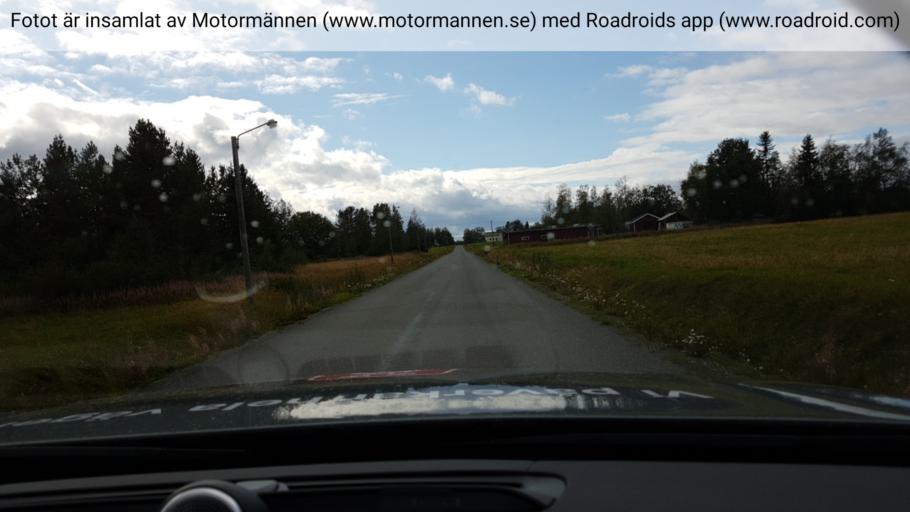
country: SE
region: Jaemtland
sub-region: OEstersunds Kommun
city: Lit
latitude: 63.6816
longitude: 14.8421
